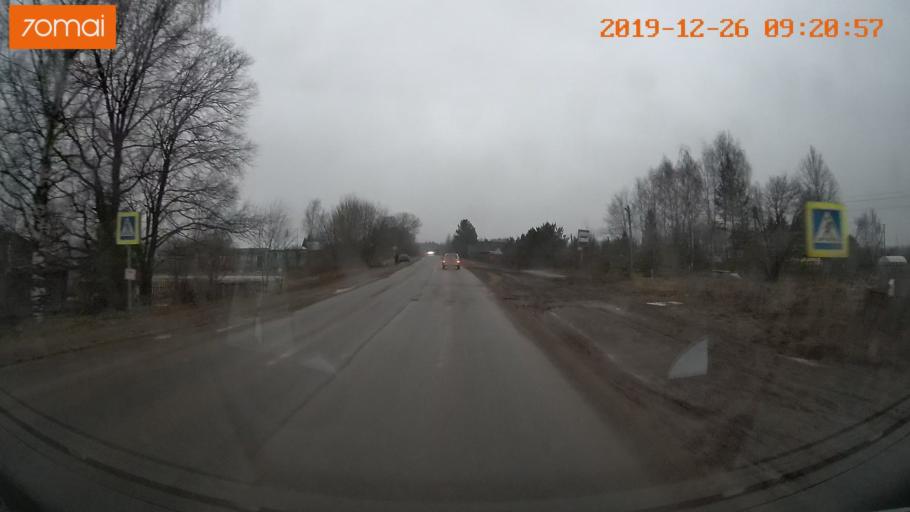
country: RU
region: Vologda
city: Gryazovets
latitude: 58.9661
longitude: 40.2270
